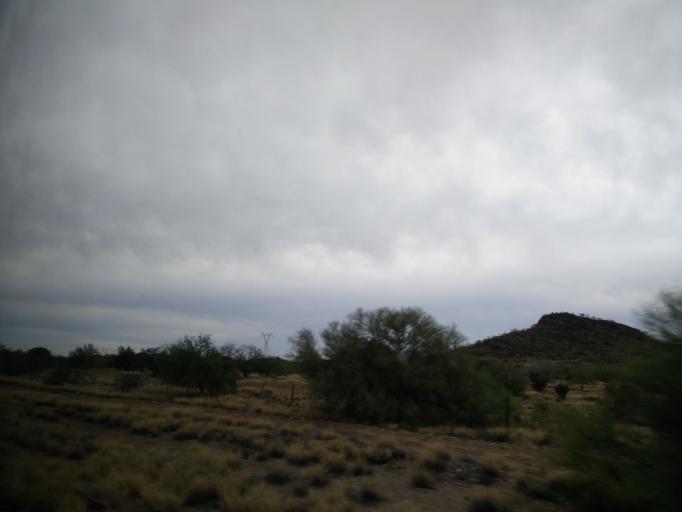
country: MX
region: Sonora
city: Hermosillo
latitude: 28.6487
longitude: -111.0057
